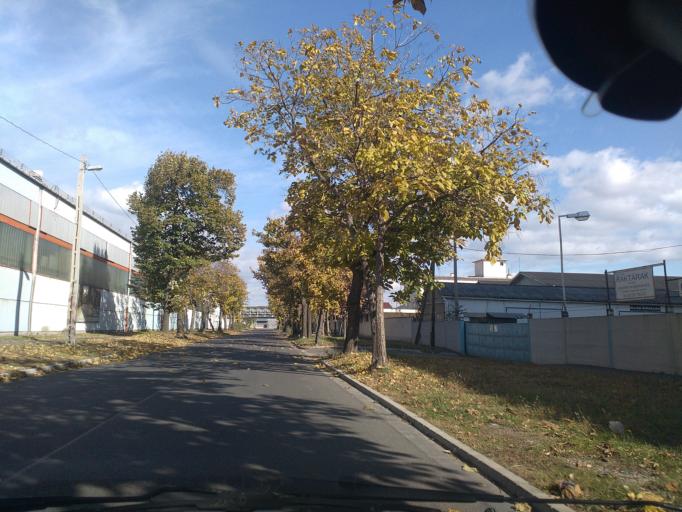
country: HU
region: Budapest
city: Budapest XIX. keruelet
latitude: 47.4716
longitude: 19.1260
